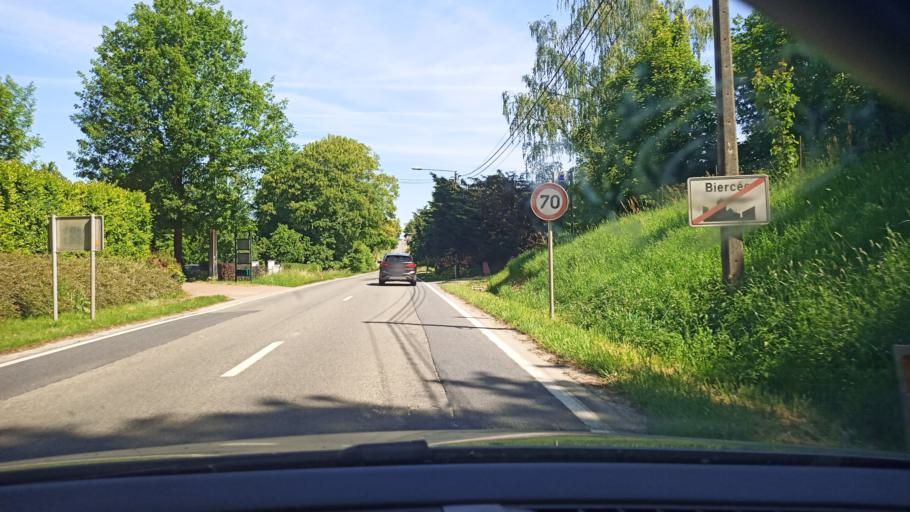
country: BE
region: Wallonia
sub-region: Province du Hainaut
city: Lobbes
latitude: 50.3305
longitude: 4.2629
